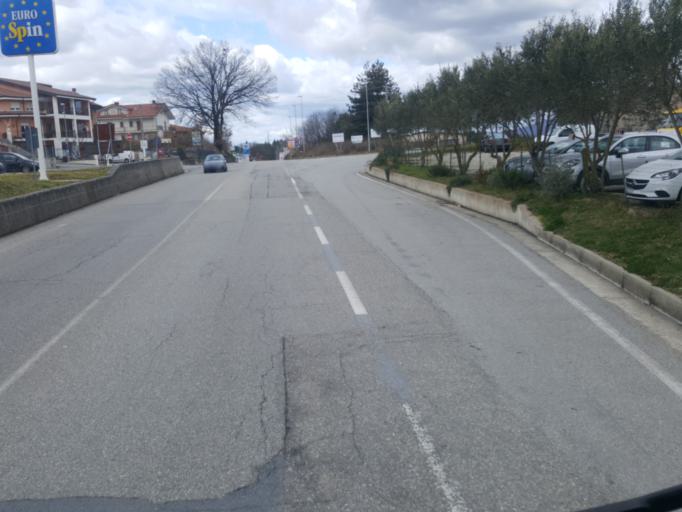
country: IT
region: Calabria
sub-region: Provincia di Cosenza
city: Piane Crati
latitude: 39.2156
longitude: 16.3076
